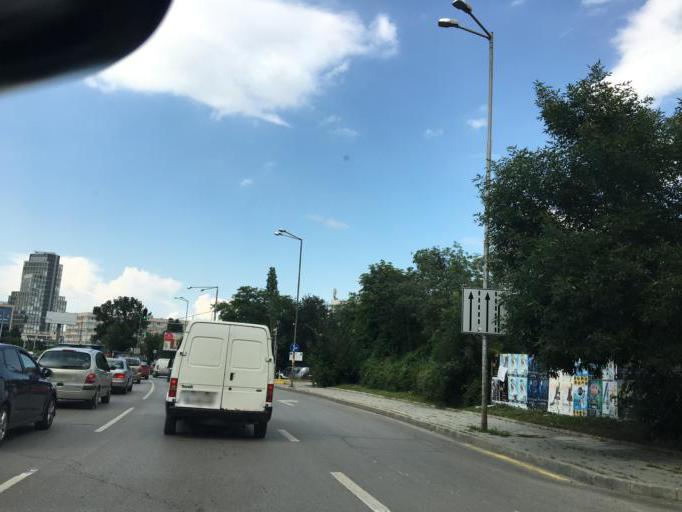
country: BG
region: Sofia-Capital
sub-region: Stolichna Obshtina
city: Sofia
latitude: 42.6612
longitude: 23.3590
